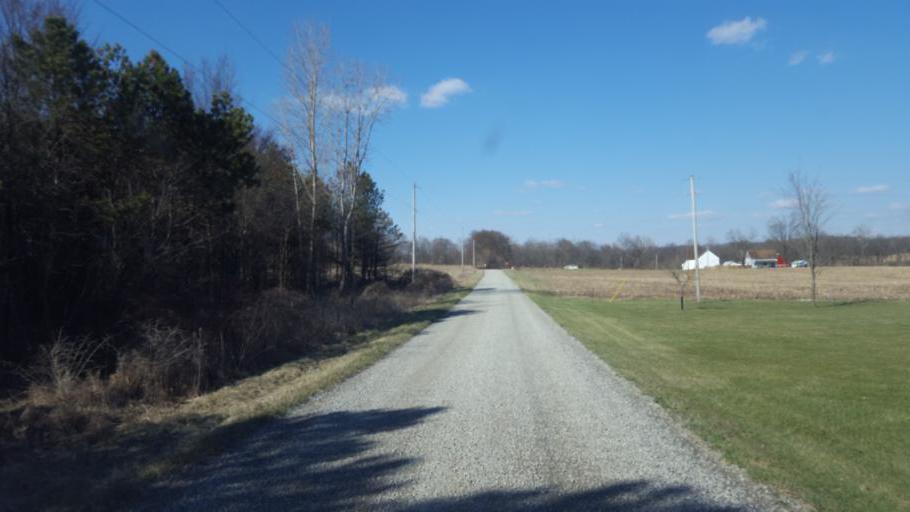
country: US
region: Ohio
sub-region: Morrow County
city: Mount Gilead
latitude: 40.4720
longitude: -82.7444
